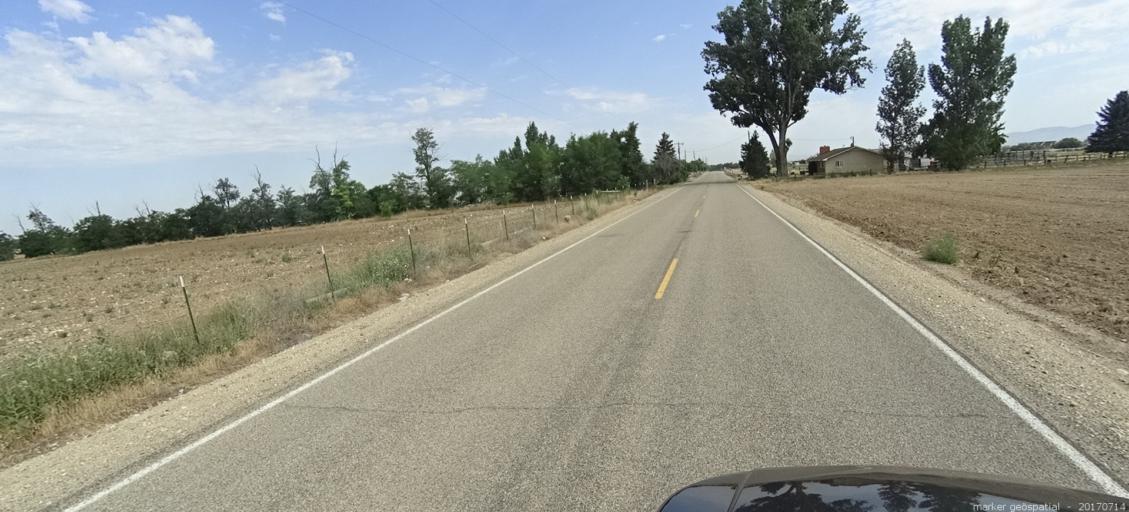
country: US
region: Idaho
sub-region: Ada County
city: Kuna
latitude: 43.4947
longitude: -116.3543
